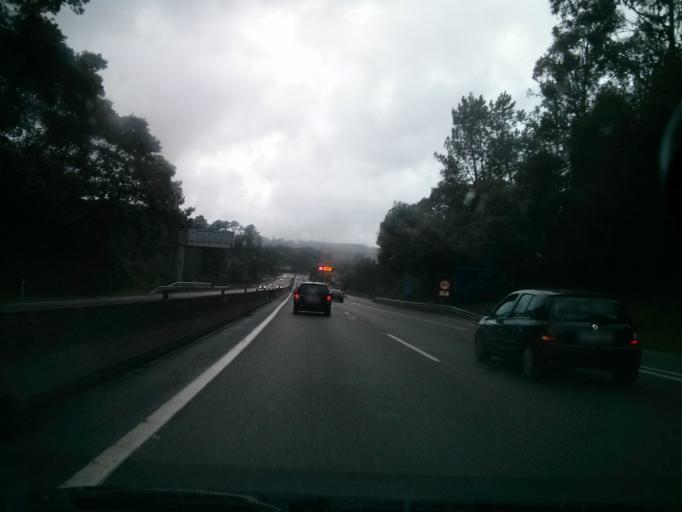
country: ES
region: Galicia
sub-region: Provincia de Pontevedra
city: Porrino
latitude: 42.1815
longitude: -8.6286
